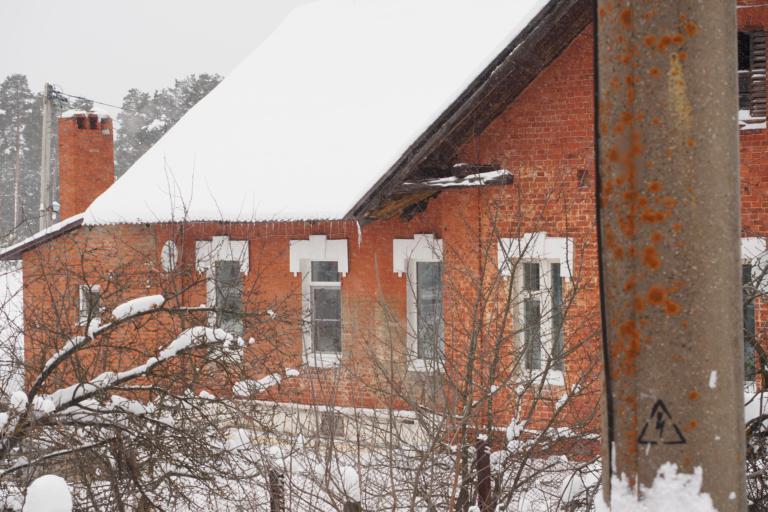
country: RU
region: Moskovskaya
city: Khorlovo
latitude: 55.3401
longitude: 38.8117
